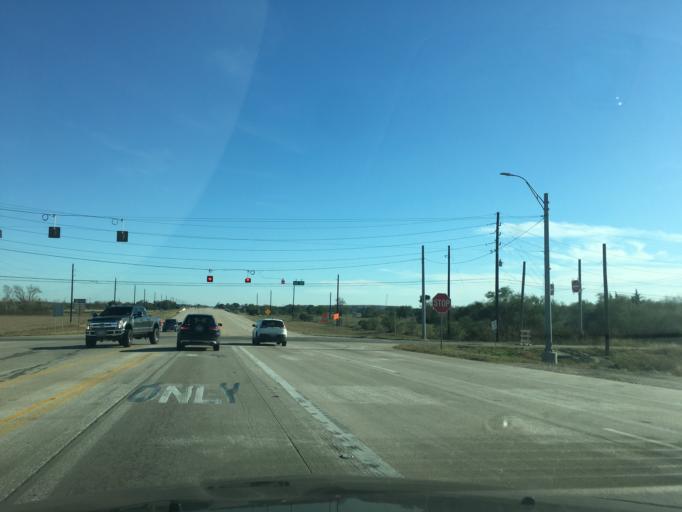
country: US
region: Texas
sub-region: Fort Bend County
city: Rosenberg
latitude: 29.5227
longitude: -95.8728
